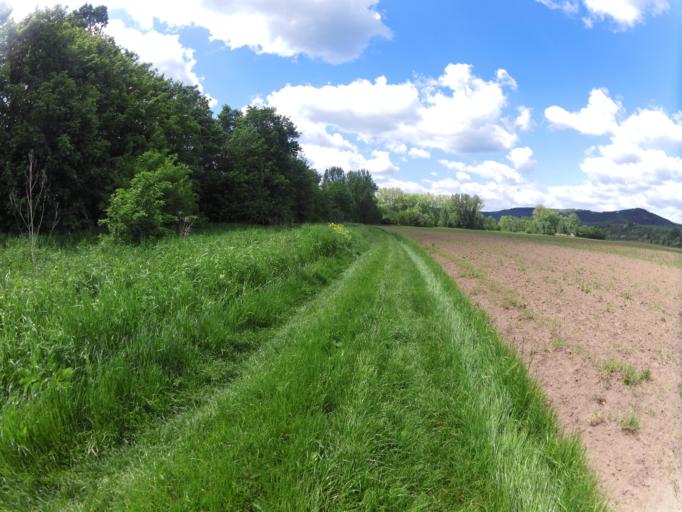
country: DE
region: Thuringia
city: Treffurt
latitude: 51.1141
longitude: 10.2500
